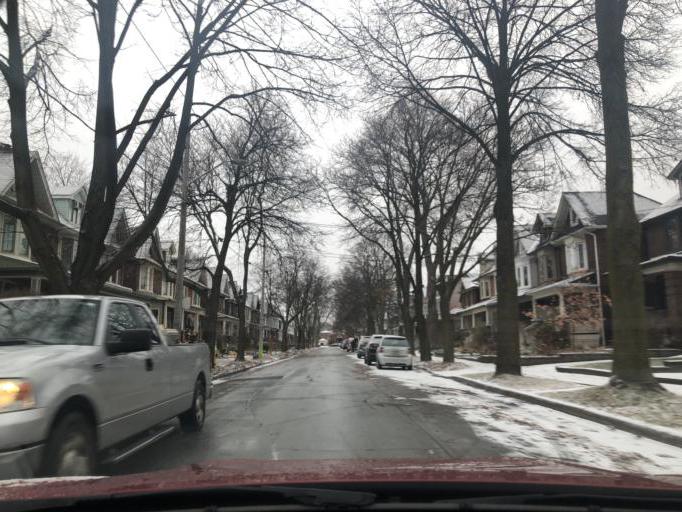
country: CA
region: Ontario
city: Toronto
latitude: 43.6821
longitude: -79.3416
